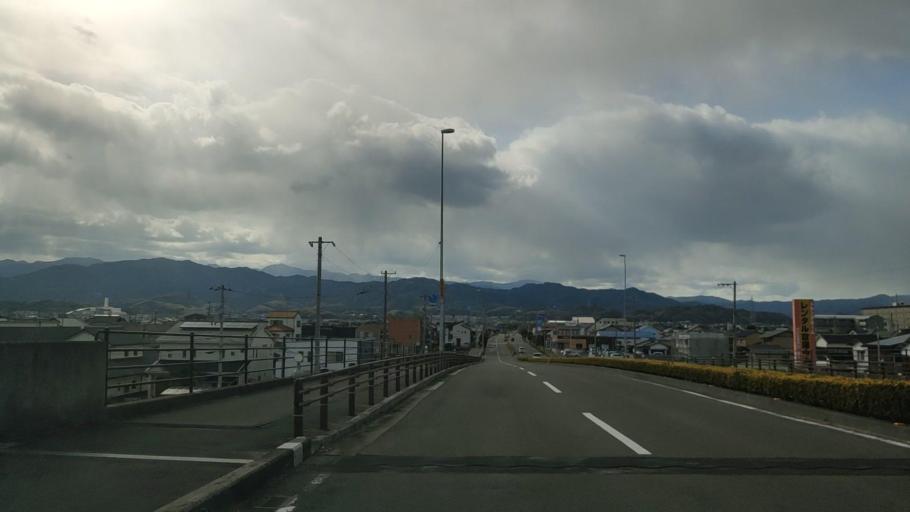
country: JP
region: Ehime
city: Saijo
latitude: 34.0444
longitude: 133.0048
